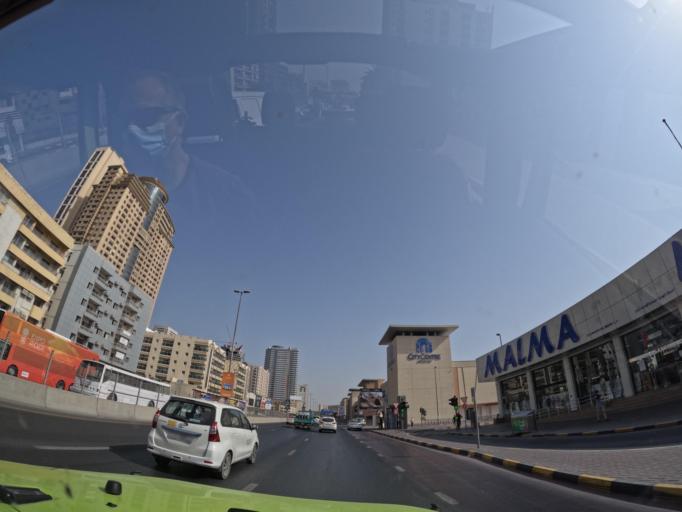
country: AE
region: Ash Shariqah
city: Sharjah
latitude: 25.3243
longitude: 55.3917
